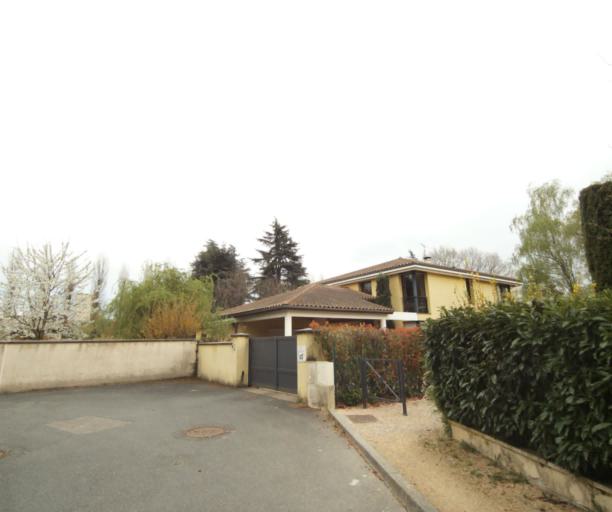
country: FR
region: Bourgogne
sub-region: Departement de Saone-et-Loire
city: Macon
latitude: 46.3041
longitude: 4.8120
